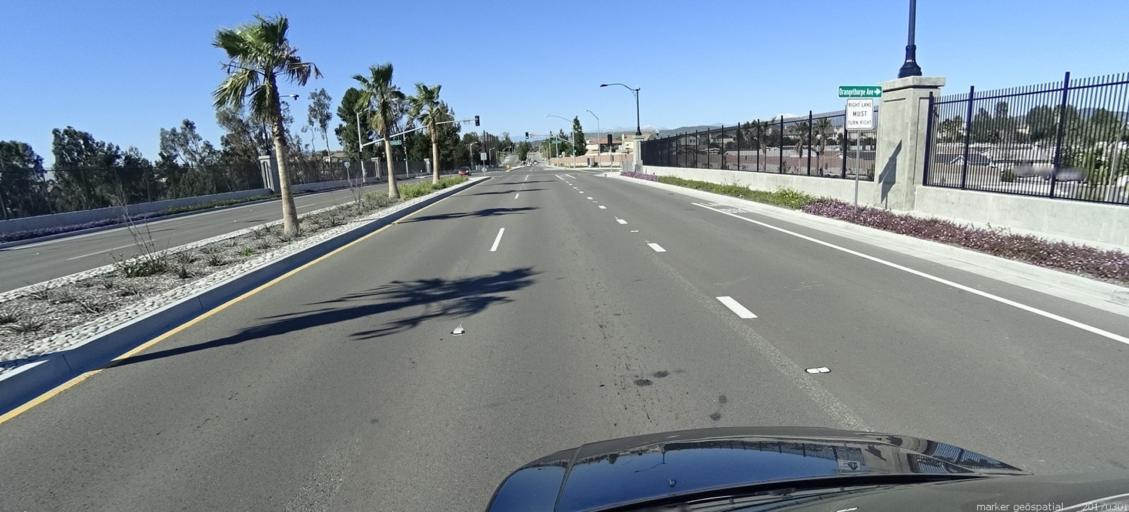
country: US
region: California
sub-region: Orange County
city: Placentia
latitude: 33.8686
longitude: -117.8426
